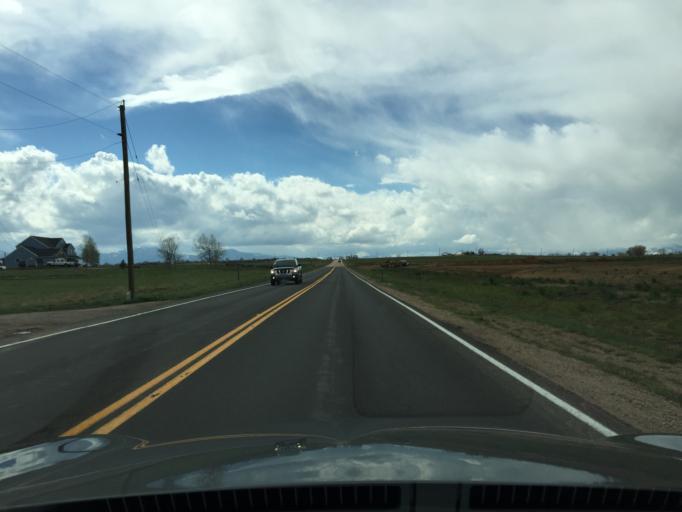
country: US
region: Colorado
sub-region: Boulder County
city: Lafayette
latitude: 40.0148
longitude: -105.0623
